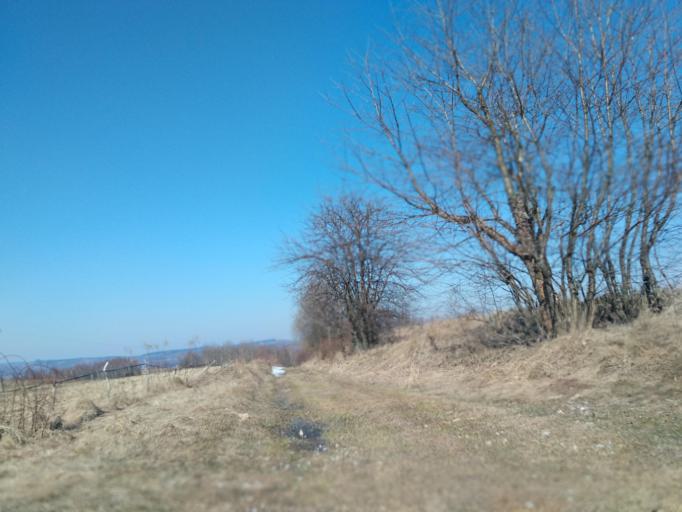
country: PL
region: Subcarpathian Voivodeship
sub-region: Powiat brzozowski
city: Golcowa
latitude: 49.7544
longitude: 22.0356
